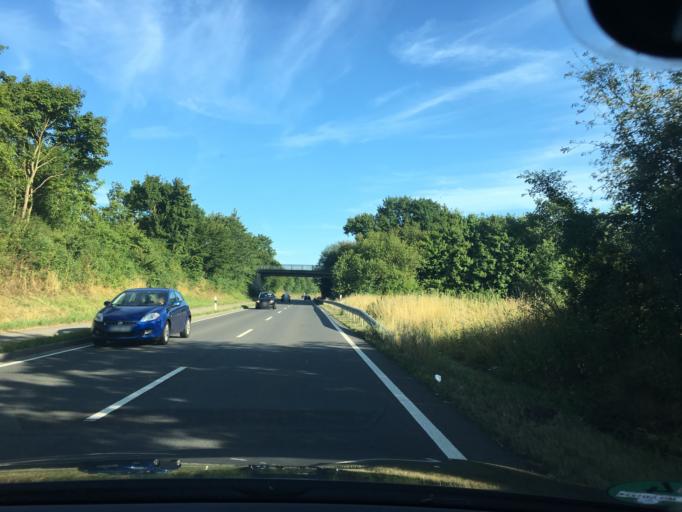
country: DE
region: North Rhine-Westphalia
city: Julich
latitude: 50.9224
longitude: 6.4166
